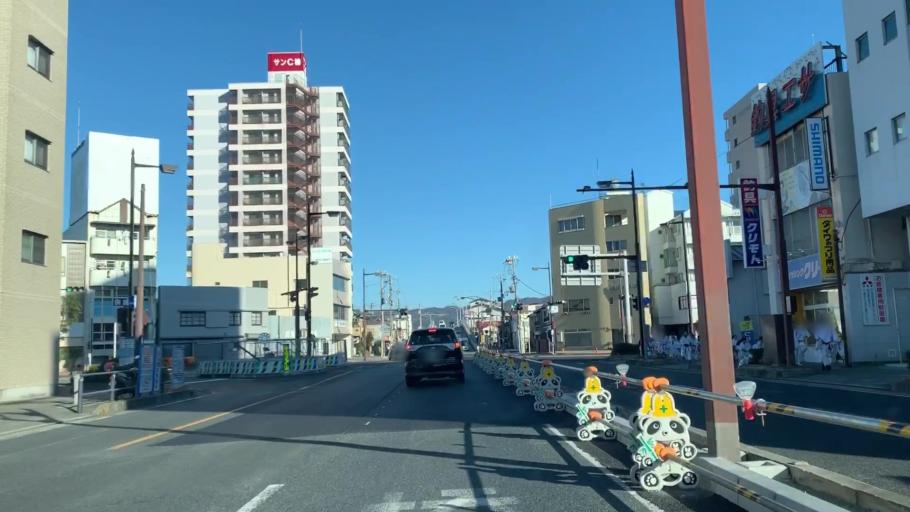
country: JP
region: Wakayama
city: Wakayama-shi
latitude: 34.2366
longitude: 135.1695
